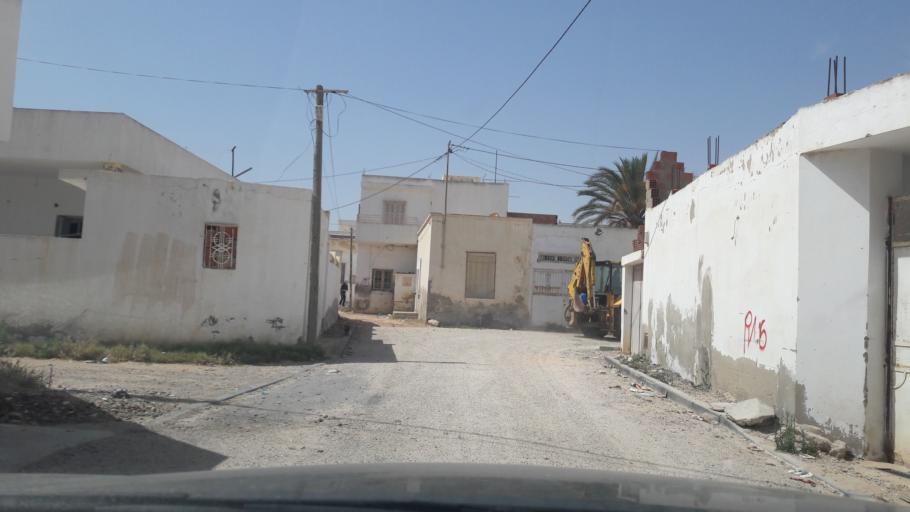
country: TN
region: Safaqis
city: Al Qarmadah
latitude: 34.7767
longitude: 10.7686
